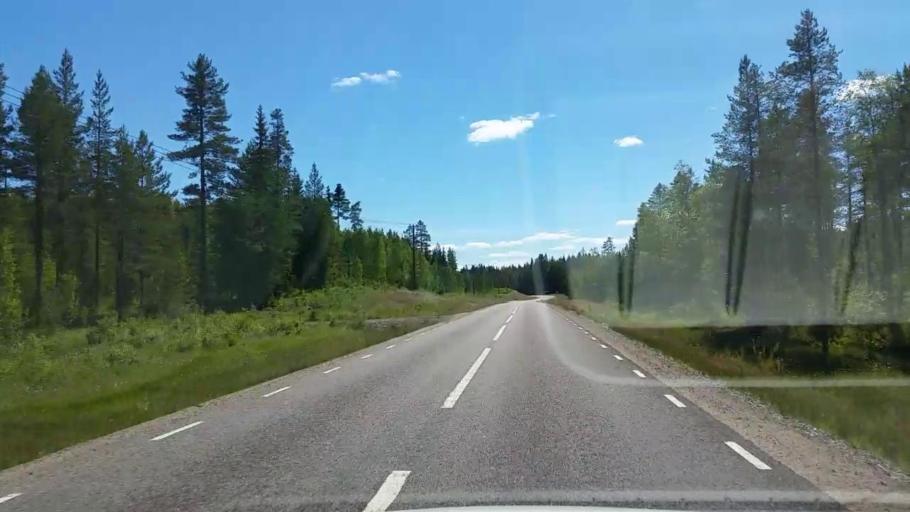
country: SE
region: Gaevleborg
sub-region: Ovanakers Kommun
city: Edsbyn
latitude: 61.5183
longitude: 15.6785
